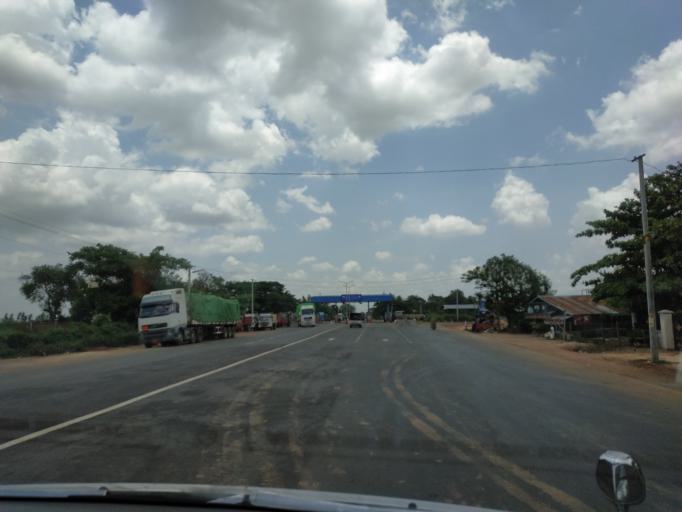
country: MM
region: Bago
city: Bago
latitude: 17.4717
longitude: 96.5453
